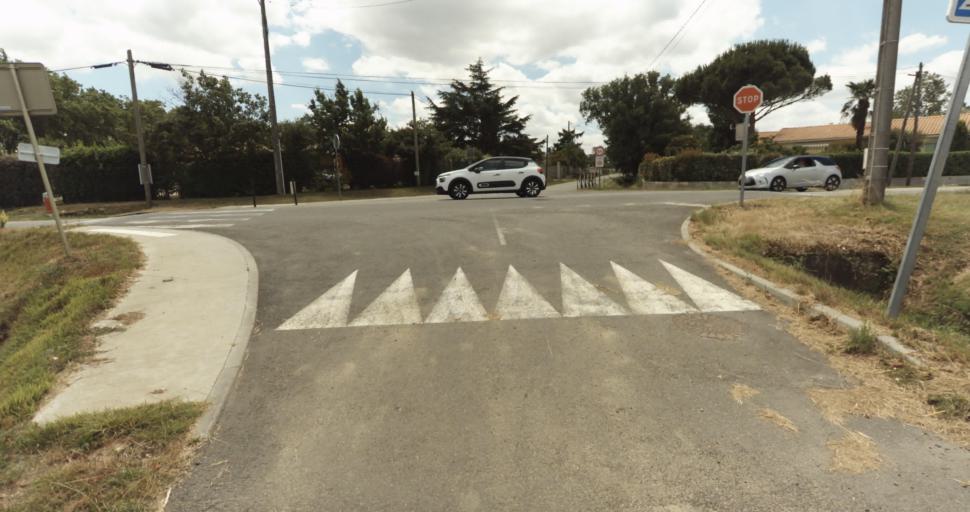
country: FR
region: Midi-Pyrenees
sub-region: Departement de la Haute-Garonne
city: Fontenilles
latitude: 43.5461
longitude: 1.1861
